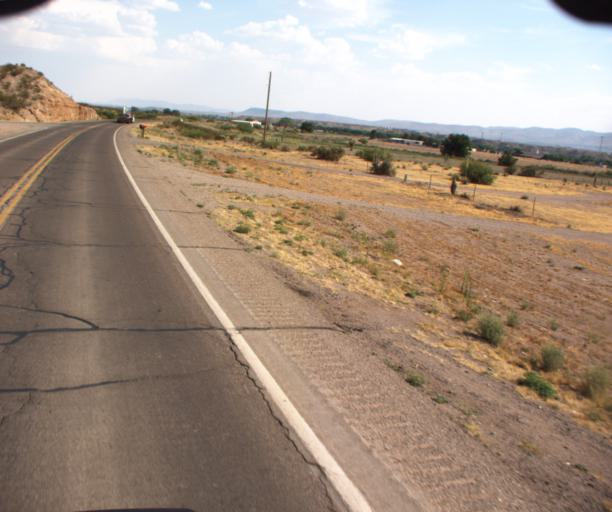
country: US
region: Arizona
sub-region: Greenlee County
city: Clifton
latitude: 32.7353
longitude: -109.0926
